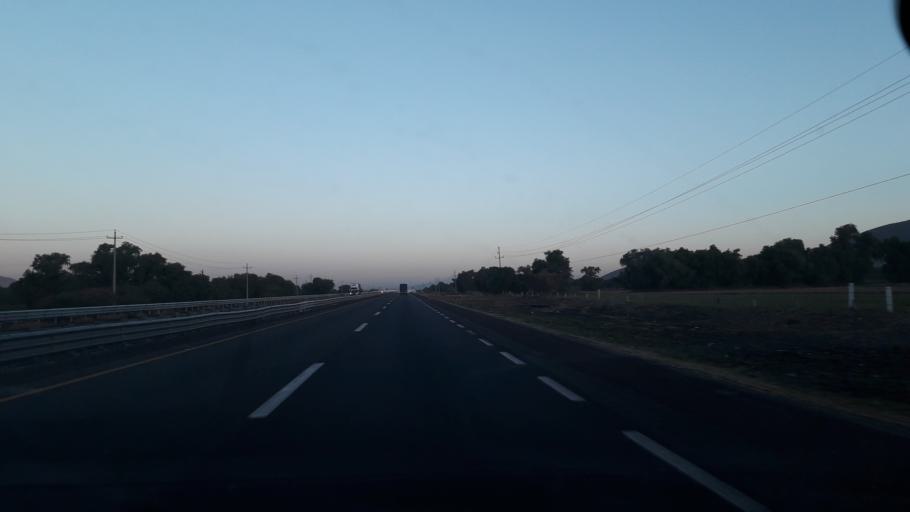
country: MX
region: Puebla
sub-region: Palmar de Bravo
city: Bellavista de Victoria (San Jose Bellavista)
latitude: 18.8625
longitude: -97.5568
